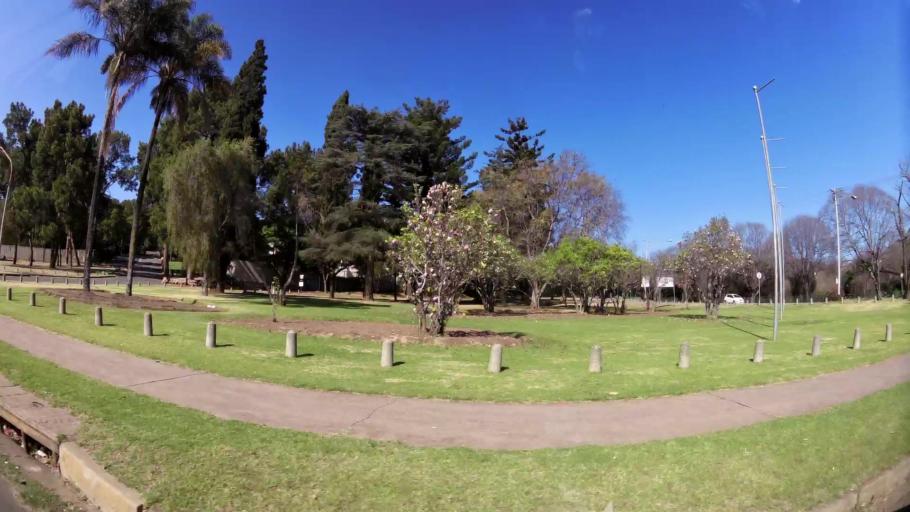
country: ZA
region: Gauteng
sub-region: City of Tshwane Metropolitan Municipality
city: Pretoria
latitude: -25.7606
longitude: 28.2201
